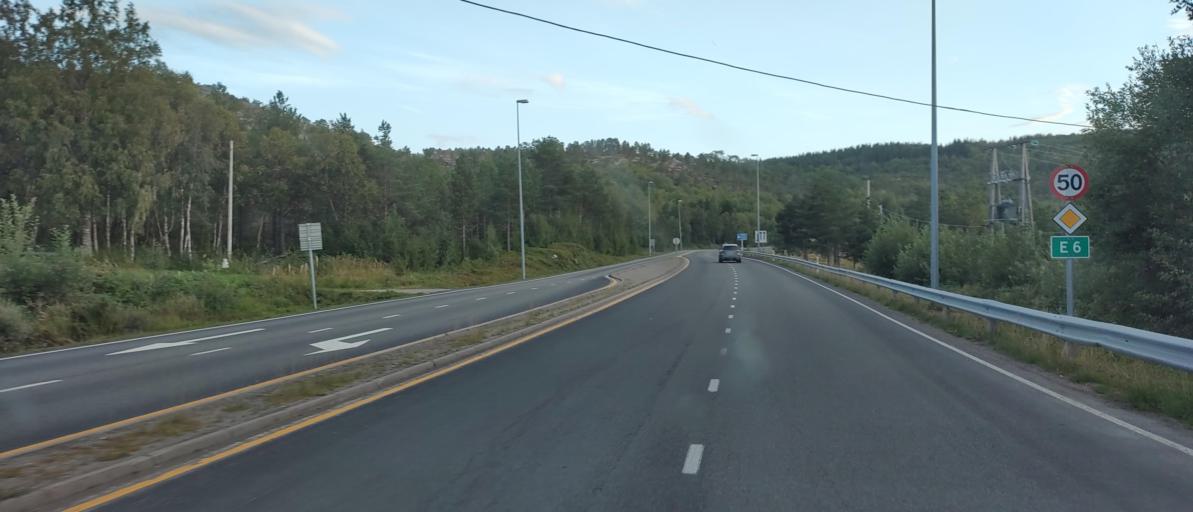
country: NO
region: Nordland
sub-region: Lodingen
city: Lodingen
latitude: 68.2215
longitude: 16.0713
